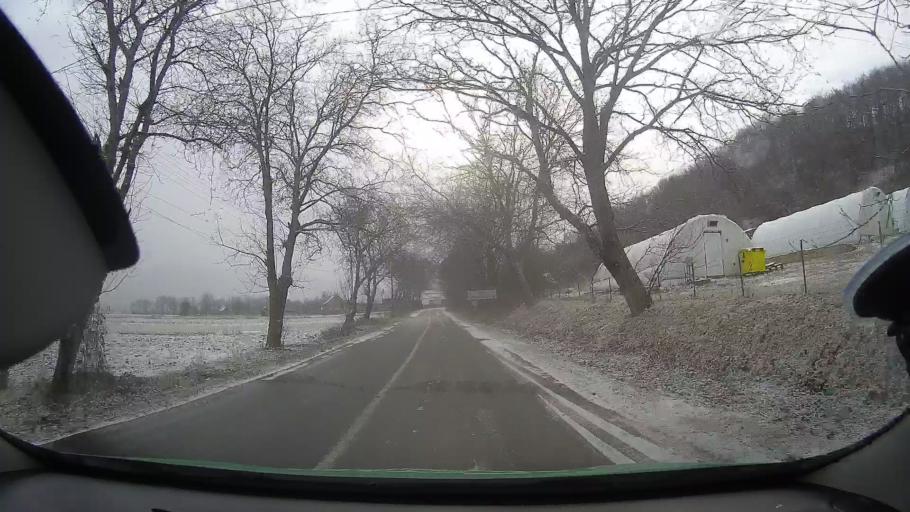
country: RO
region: Alba
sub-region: Comuna Rimetea
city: Rimetea
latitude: 46.4274
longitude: 23.5612
